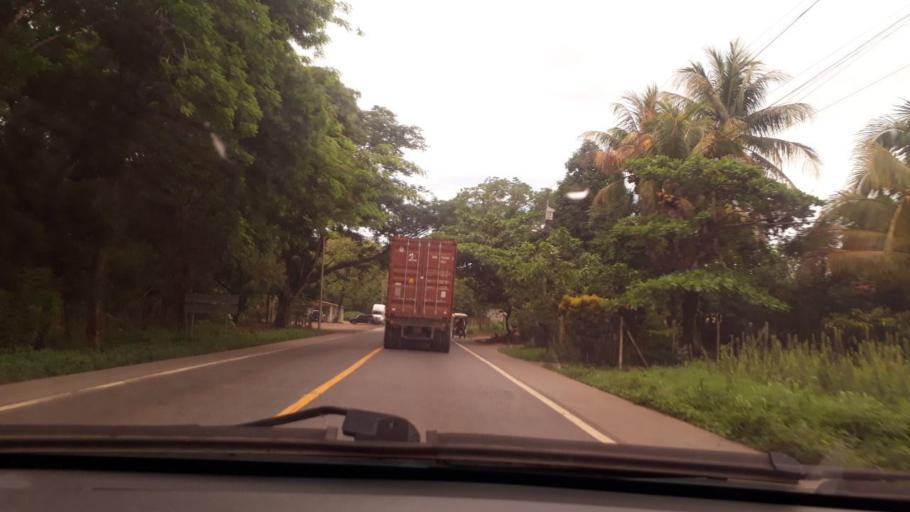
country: GT
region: Izabal
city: Morales
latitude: 15.5532
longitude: -88.6857
